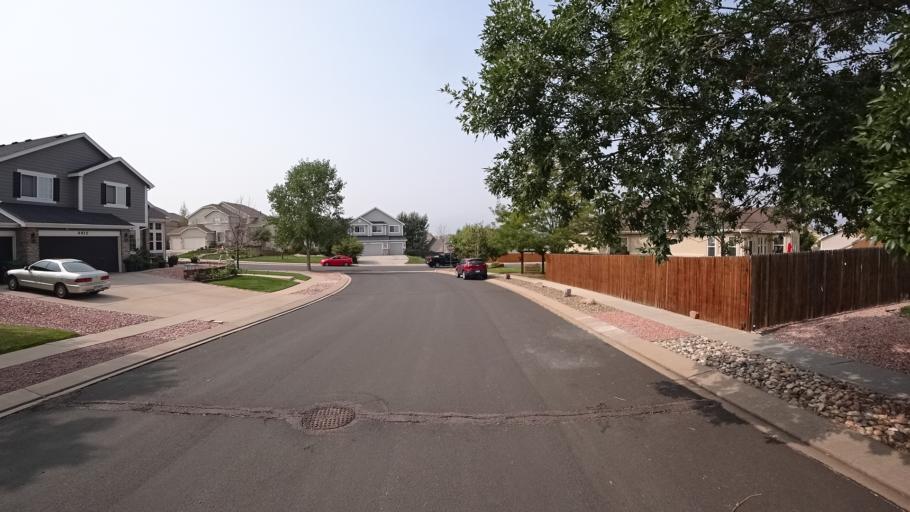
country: US
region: Colorado
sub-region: El Paso County
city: Cimarron Hills
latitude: 38.9250
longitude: -104.7441
